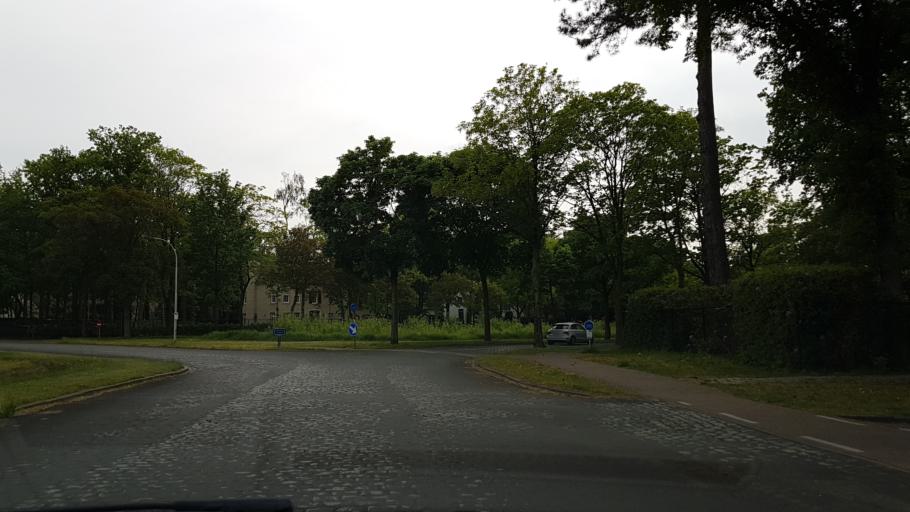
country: BE
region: Flanders
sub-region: Provincie Antwerpen
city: Brasschaat
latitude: 51.2903
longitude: 4.4647
